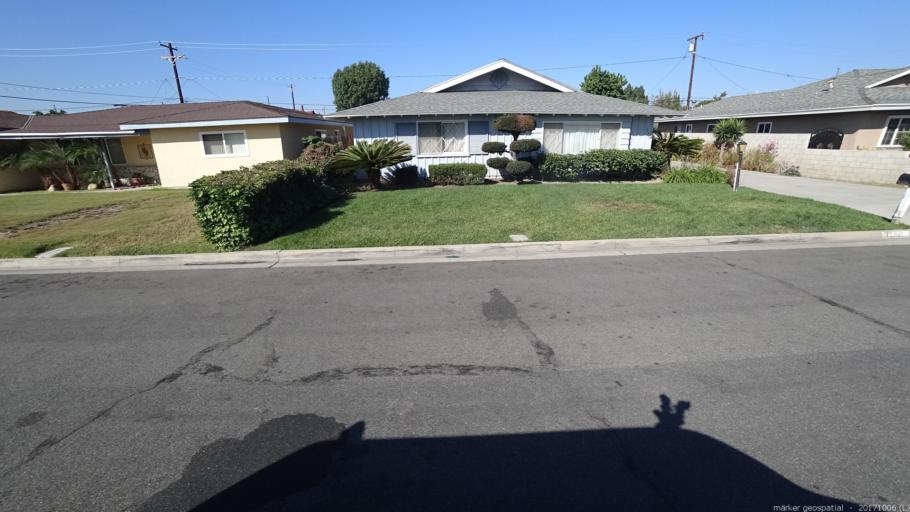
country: US
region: California
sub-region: Orange County
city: Stanton
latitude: 33.7835
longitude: -117.9823
